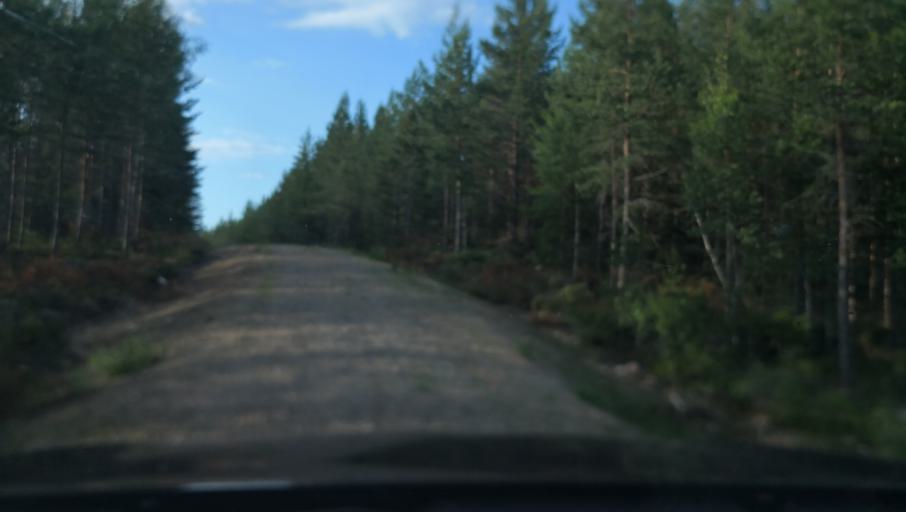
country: SE
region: Dalarna
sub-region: Smedjebackens Kommun
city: Smedjebacken
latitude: 60.0647
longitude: 15.3087
